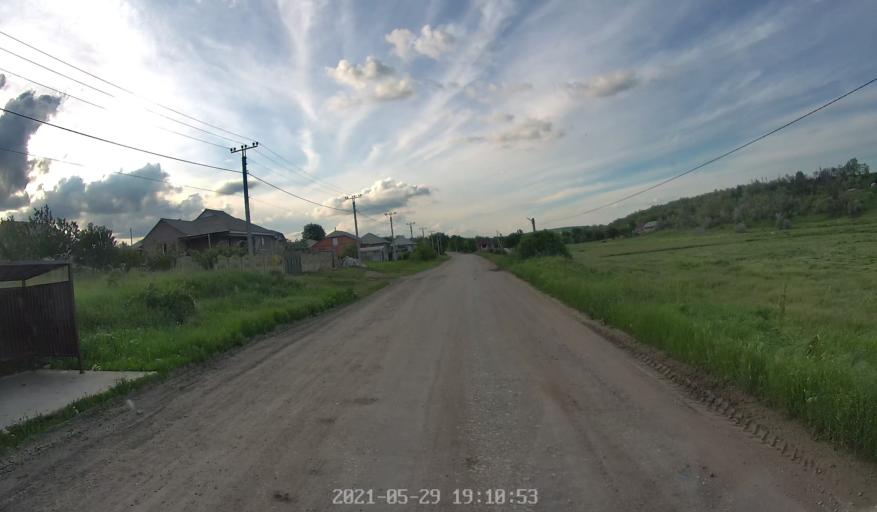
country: MD
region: Chisinau
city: Singera
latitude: 46.8350
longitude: 28.9556
